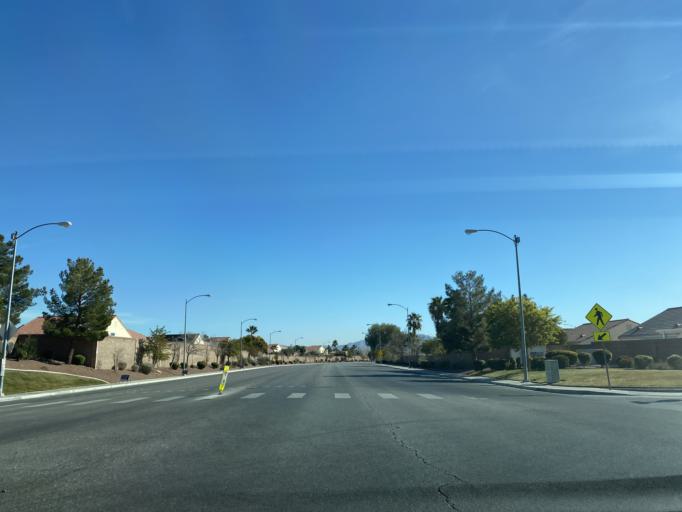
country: US
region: Nevada
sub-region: Clark County
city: North Las Vegas
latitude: 36.2822
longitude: -115.1474
